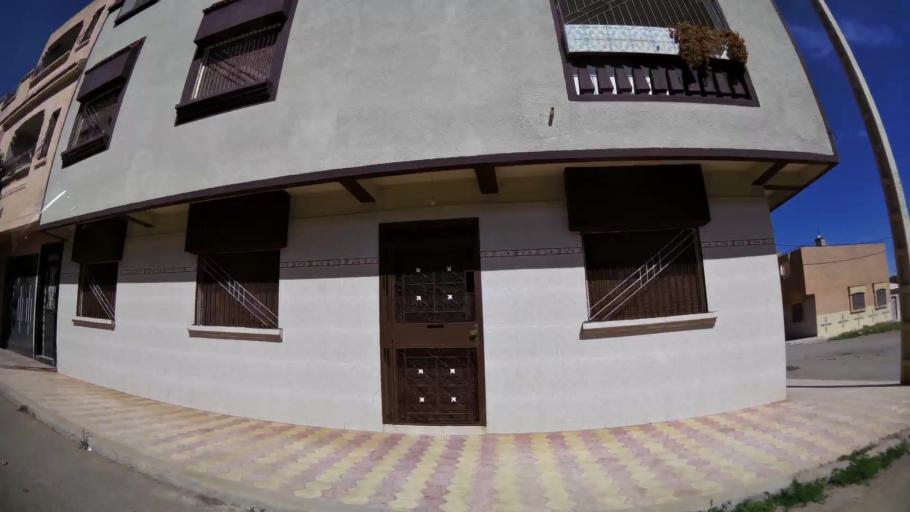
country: MA
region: Oriental
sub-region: Oujda-Angad
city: Oujda
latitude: 34.6547
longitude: -1.9329
